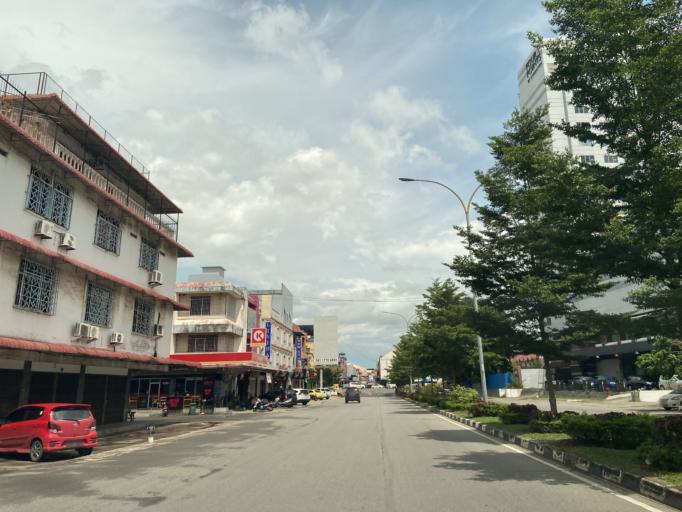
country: SG
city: Singapore
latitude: 1.1496
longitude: 104.0070
